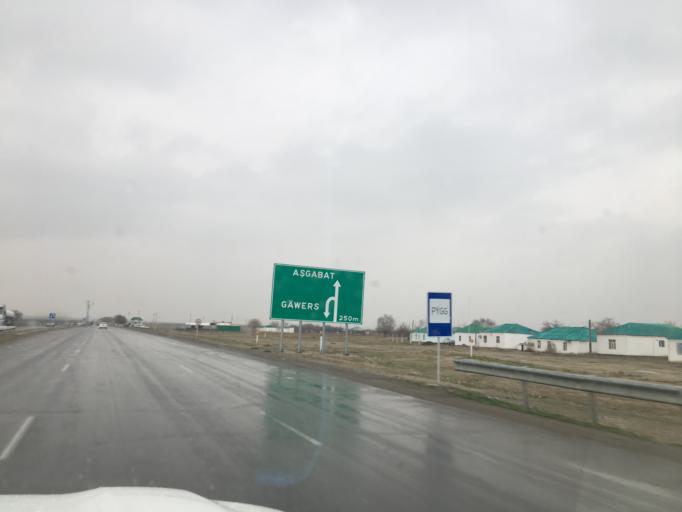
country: TM
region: Ahal
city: Annau
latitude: 37.8286
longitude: 58.7486
